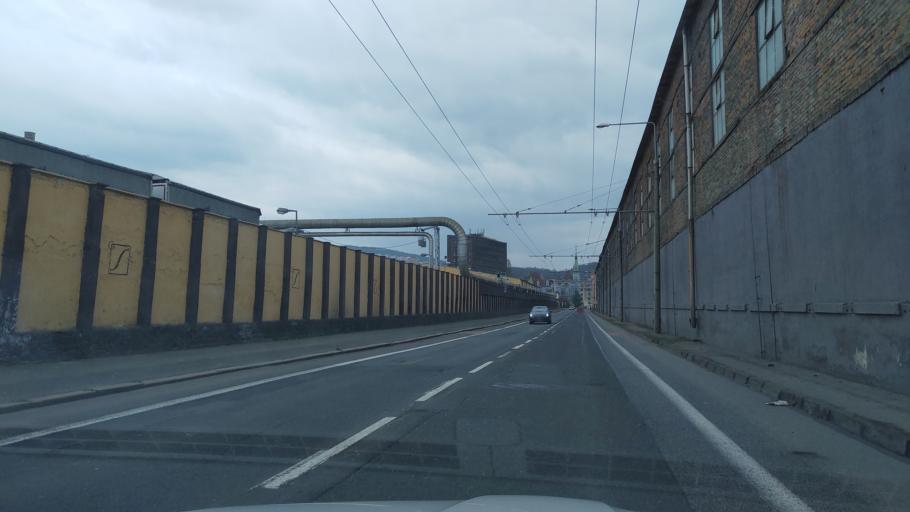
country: CZ
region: Ustecky
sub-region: Okres Usti nad Labem
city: Usti nad Labem
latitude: 50.6574
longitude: 14.0243
